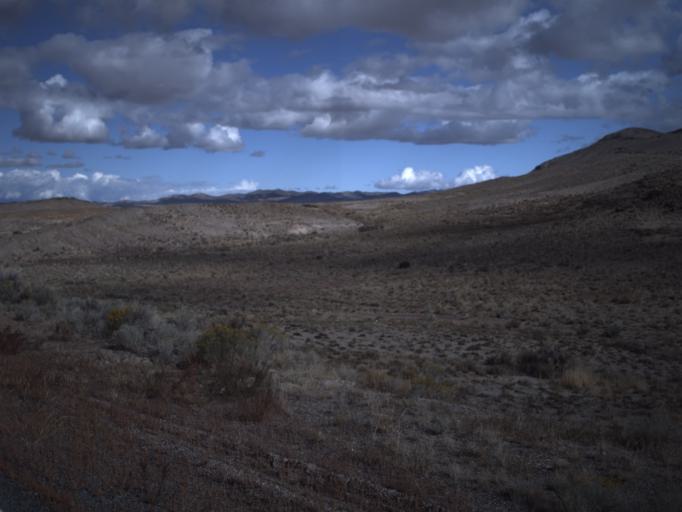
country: US
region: Utah
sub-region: Beaver County
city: Milford
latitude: 38.6174
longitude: -113.8446
